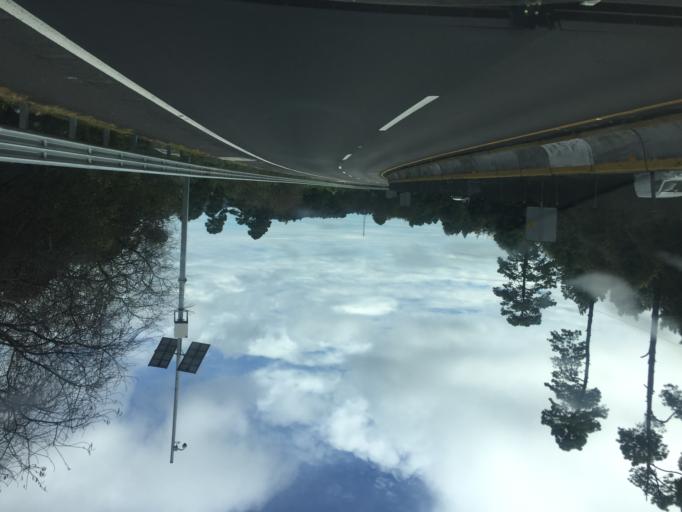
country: MX
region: Morelos
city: Tres Marias
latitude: 19.0828
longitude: -99.2312
